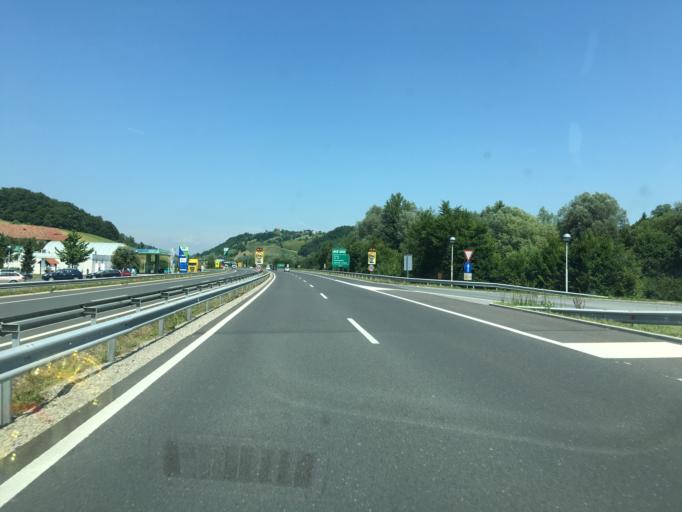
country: SI
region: Pesnica
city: Pesnica pri Mariboru
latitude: 46.6084
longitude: 15.6631
